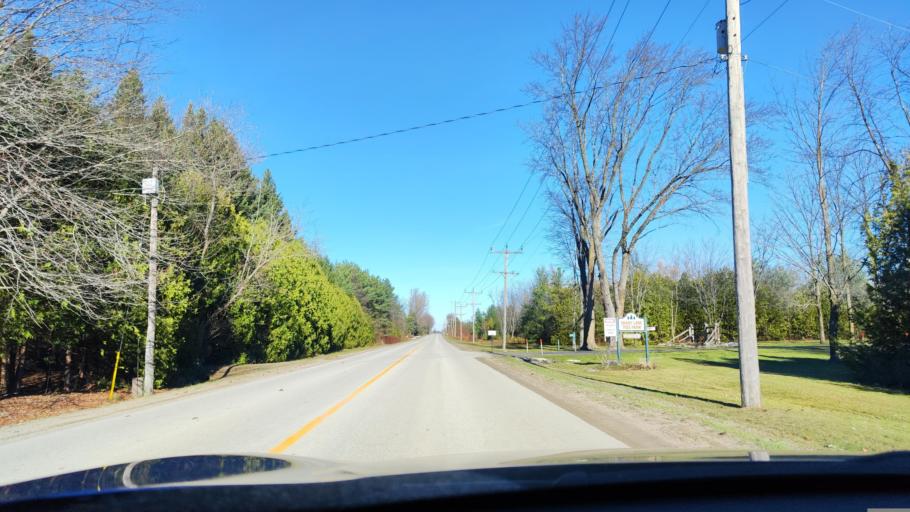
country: CA
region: Ontario
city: Collingwood
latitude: 44.4706
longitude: -80.1750
